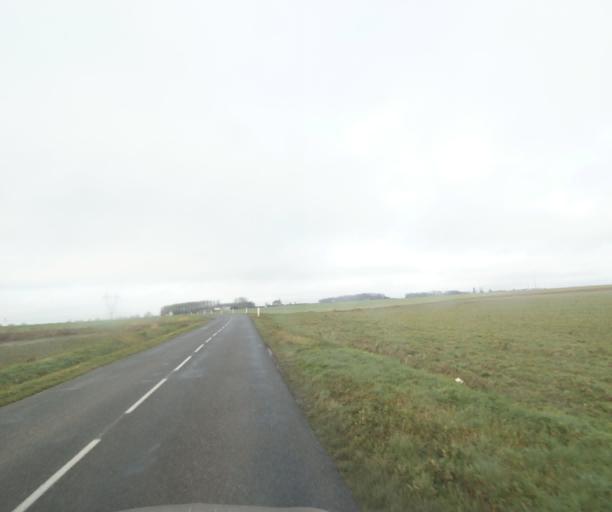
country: FR
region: Nord-Pas-de-Calais
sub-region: Departement du Nord
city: Artres
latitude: 50.2991
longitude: 3.5258
